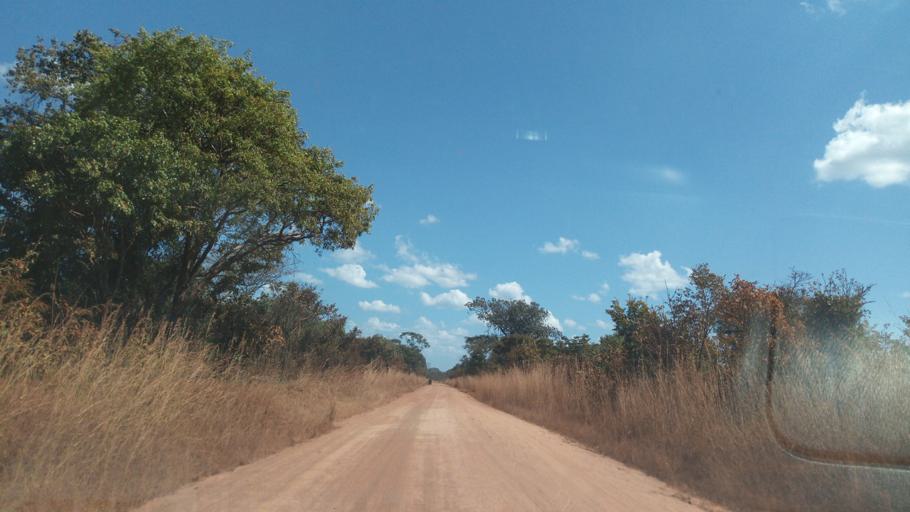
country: ZM
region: Luapula
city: Mwense
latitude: -10.7416
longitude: 28.2531
